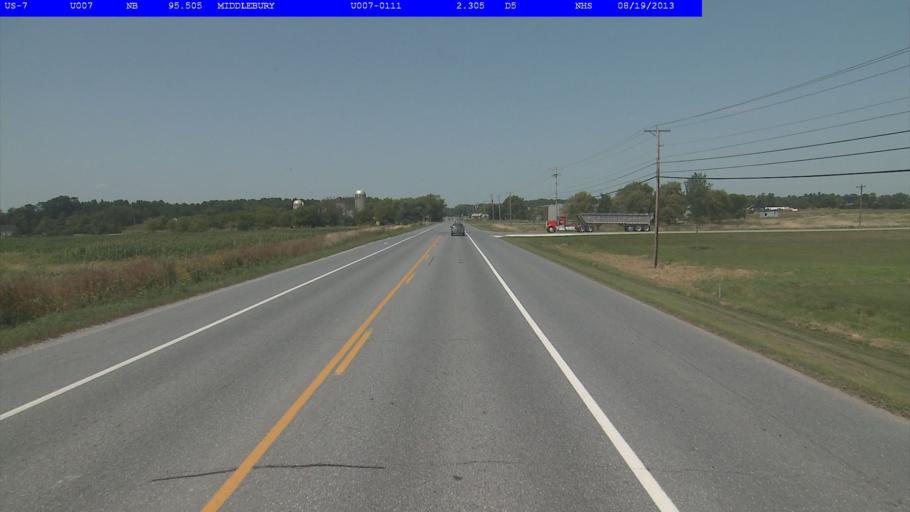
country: US
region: Vermont
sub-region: Addison County
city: Middlebury (village)
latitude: 43.9851
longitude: -73.1309
